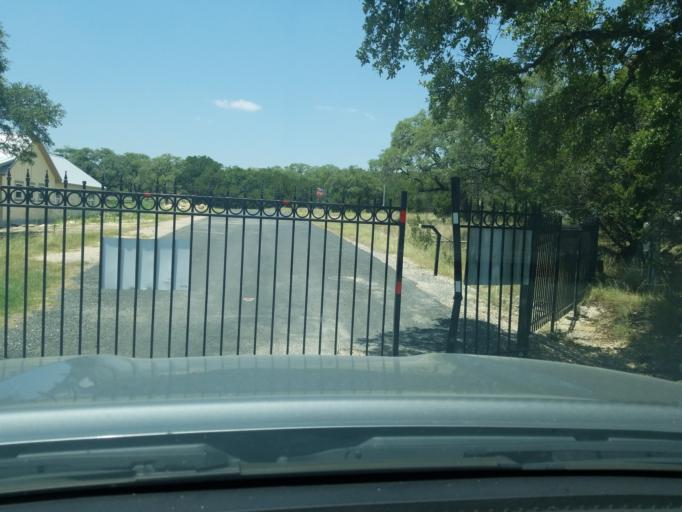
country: US
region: Texas
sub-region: Bexar County
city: Timberwood Park
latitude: 29.6969
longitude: -98.4908
